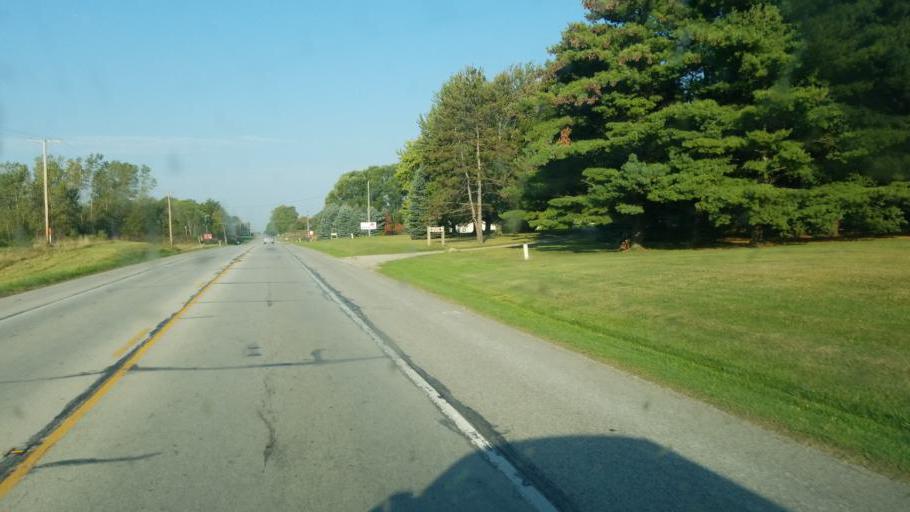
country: US
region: Indiana
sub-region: LaGrange County
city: Lagrange
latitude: 41.6414
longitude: -85.4394
